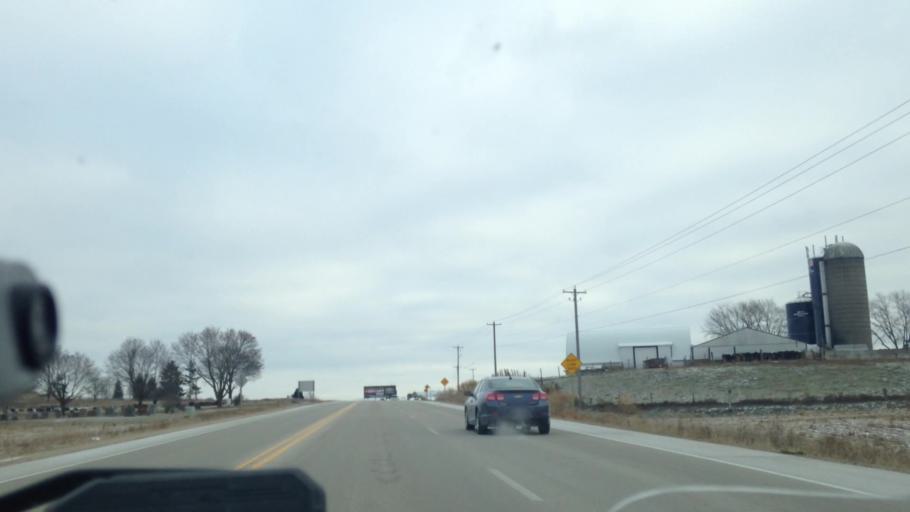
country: US
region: Wisconsin
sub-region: Washington County
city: Slinger
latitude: 43.4259
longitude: -88.3302
